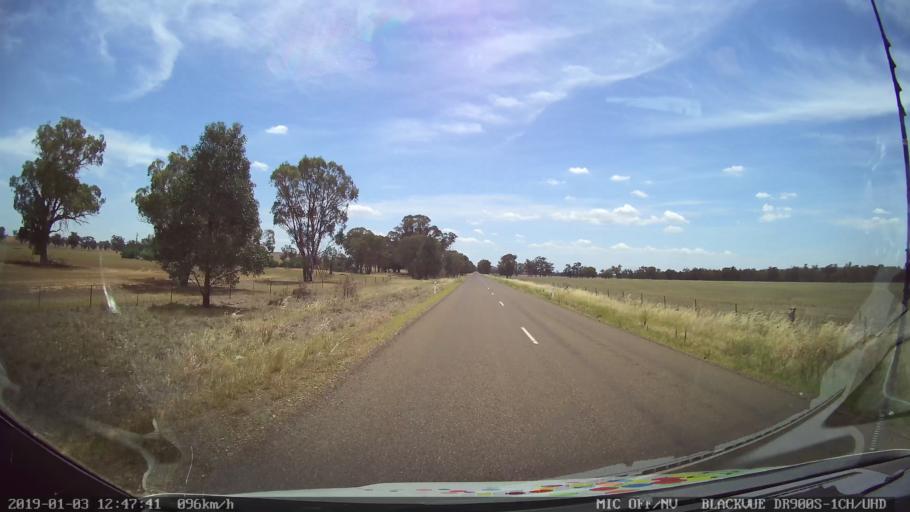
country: AU
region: New South Wales
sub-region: Weddin
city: Grenfell
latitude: -33.7237
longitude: 148.2441
